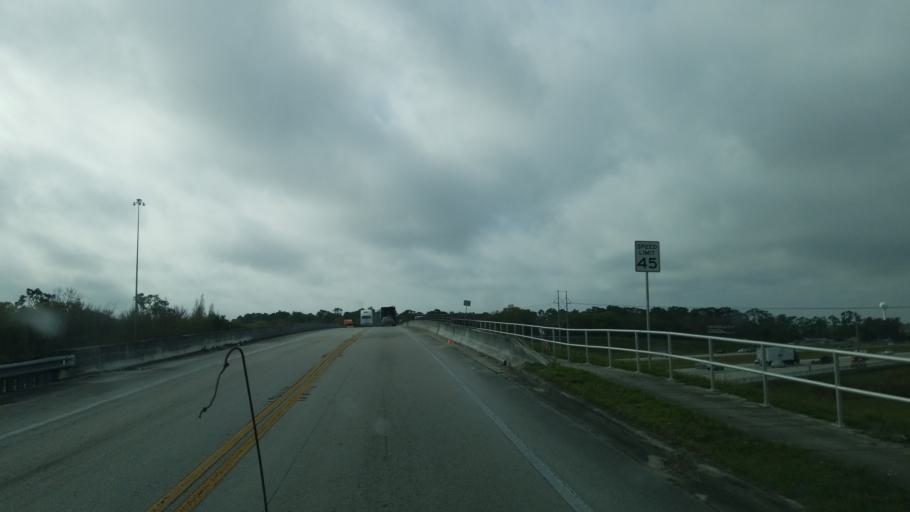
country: US
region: Florida
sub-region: Polk County
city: Winston
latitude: 28.0500
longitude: -82.0192
